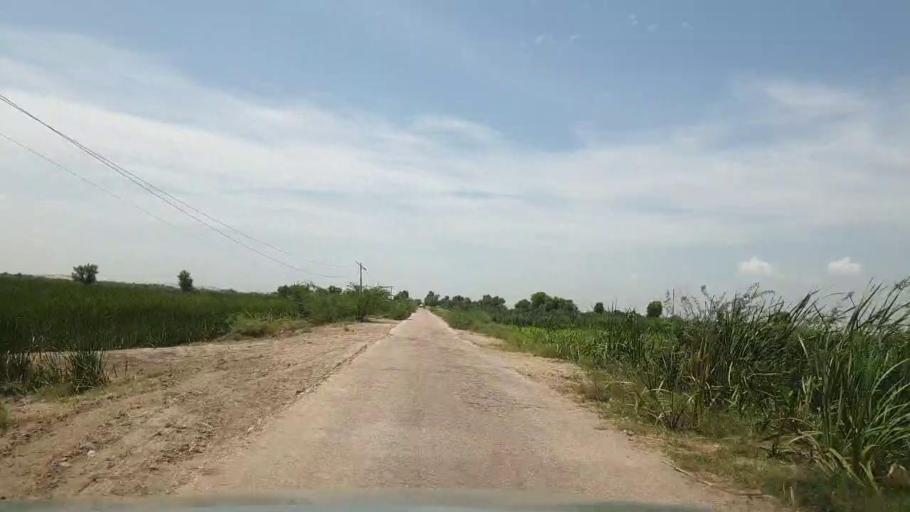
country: PK
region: Sindh
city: Bozdar
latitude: 27.0585
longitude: 68.9816
